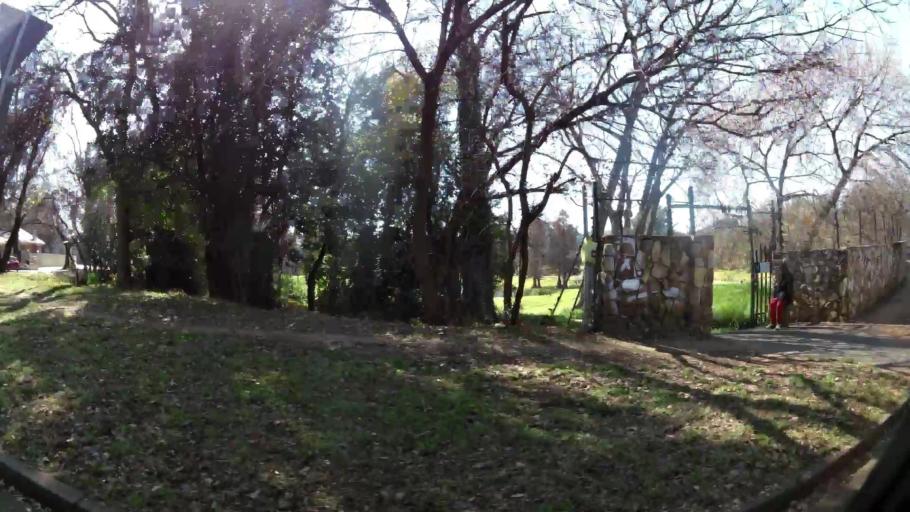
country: ZA
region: Gauteng
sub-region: City of Johannesburg Metropolitan Municipality
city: Johannesburg
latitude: -26.1512
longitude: 28.0208
